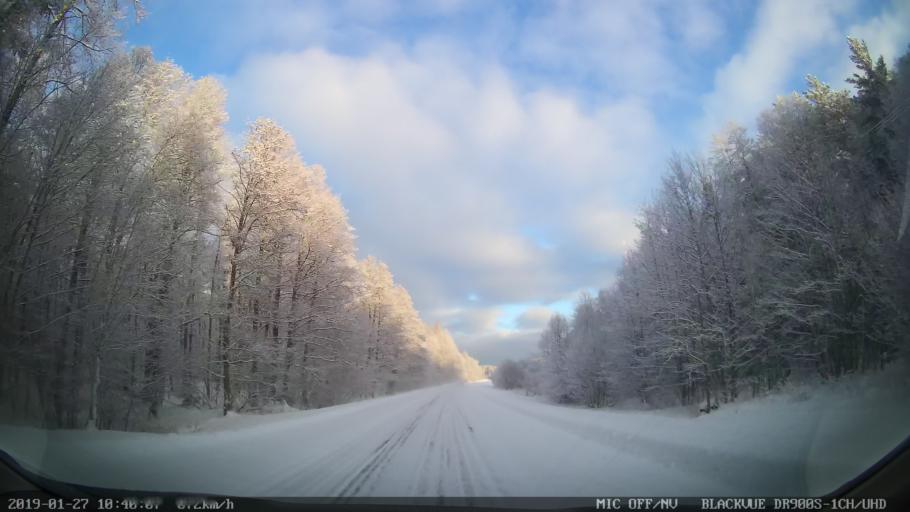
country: EE
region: Harju
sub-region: Raasiku vald
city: Raasiku
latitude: 59.4991
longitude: 25.2607
